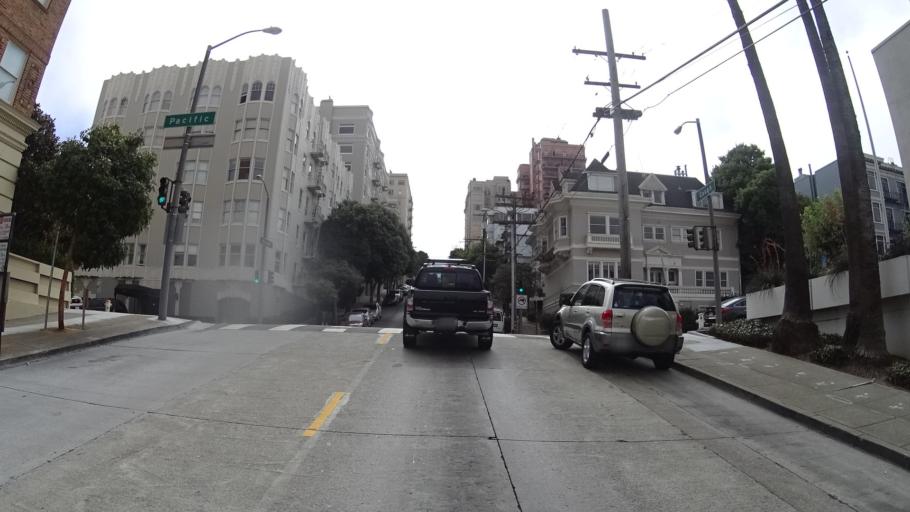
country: US
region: California
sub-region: San Francisco County
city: San Francisco
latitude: 37.7947
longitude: -122.4266
